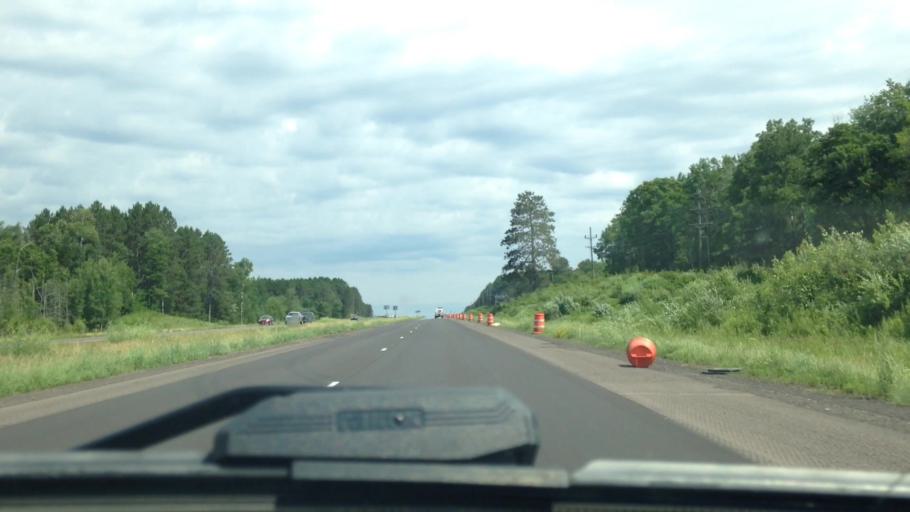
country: US
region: Wisconsin
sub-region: Washburn County
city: Spooner
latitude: 46.1463
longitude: -91.8134
